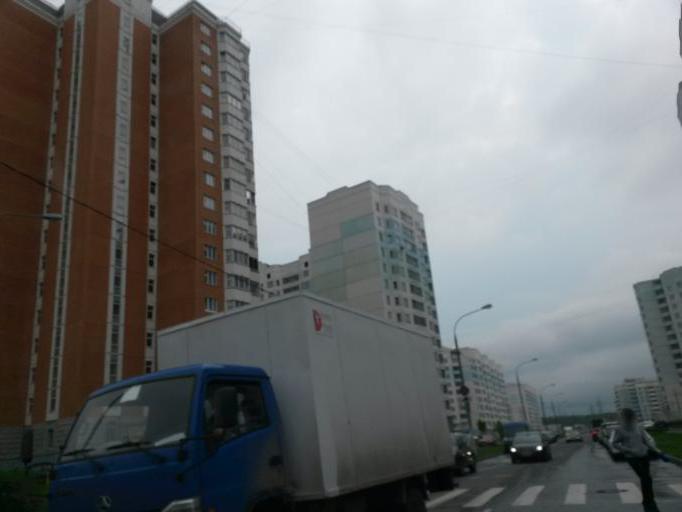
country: RU
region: Moskovskaya
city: Shcherbinka
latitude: 55.5051
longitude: 37.5931
